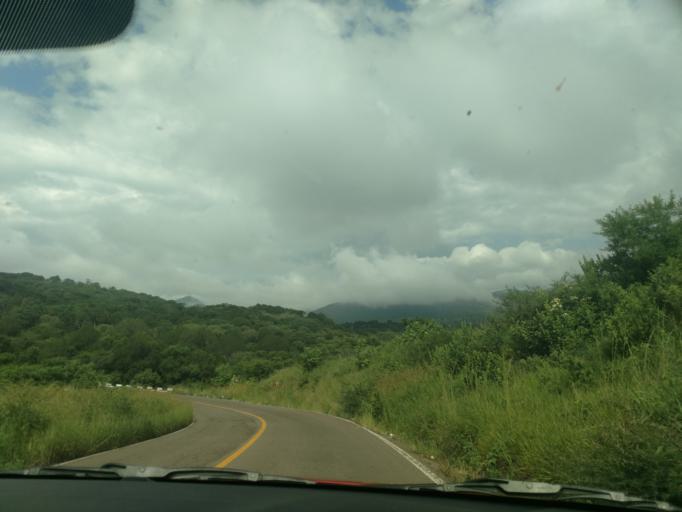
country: MX
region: Jalisco
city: El Salto
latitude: 20.3971
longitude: -104.5250
